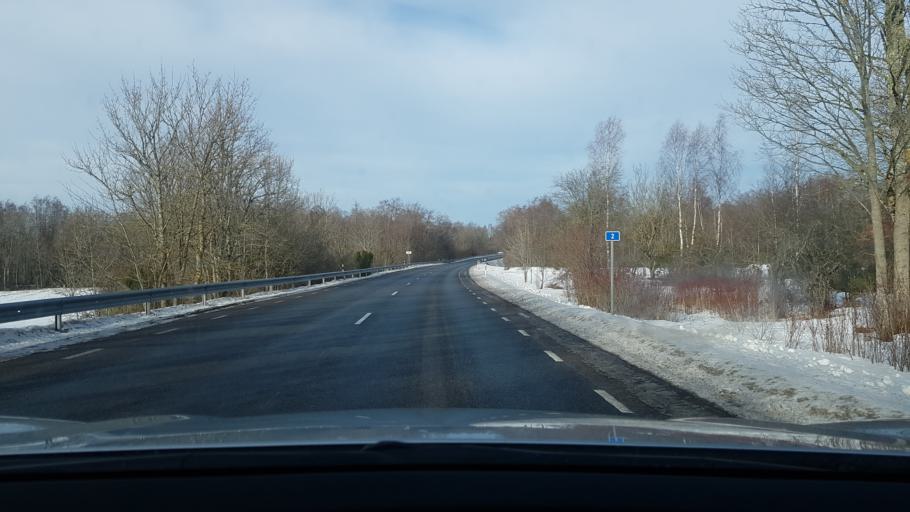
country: EE
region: Saare
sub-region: Kuressaare linn
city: Kuressaare
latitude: 58.2992
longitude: 22.5399
